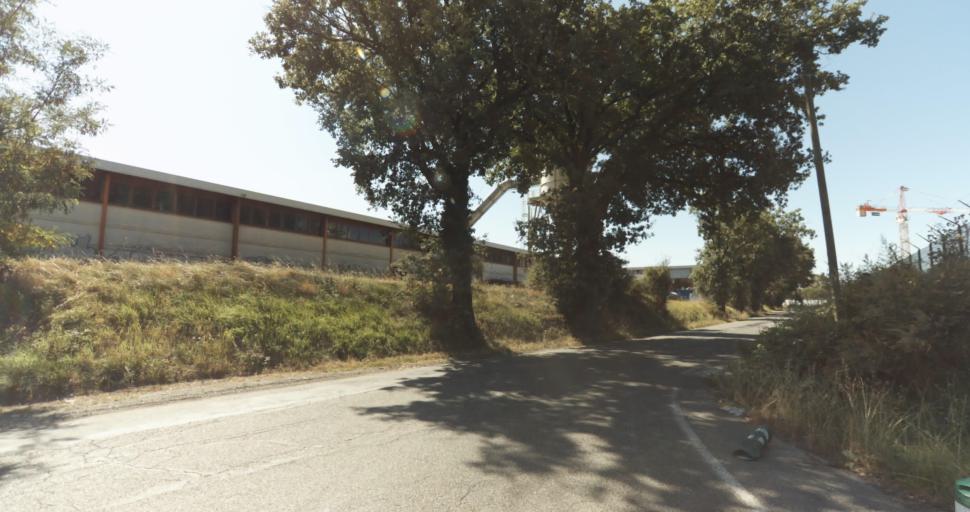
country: FR
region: Midi-Pyrenees
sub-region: Departement de la Haute-Garonne
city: L'Union
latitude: 43.6402
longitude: 1.4948
